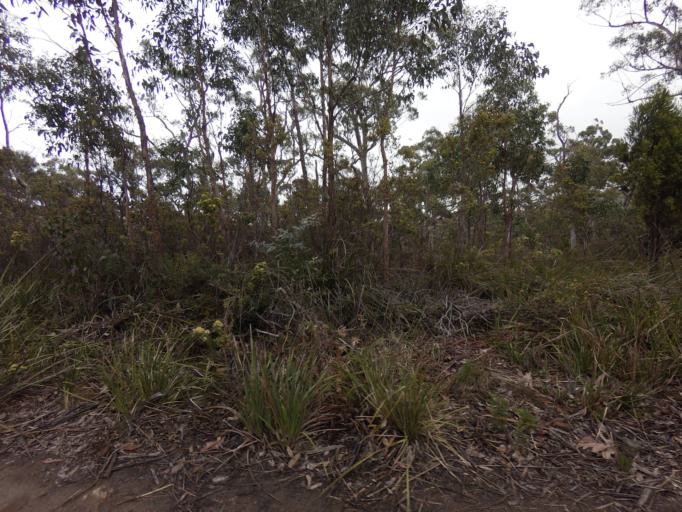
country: AU
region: Tasmania
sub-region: Huon Valley
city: Geeveston
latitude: -43.4741
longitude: 146.9344
